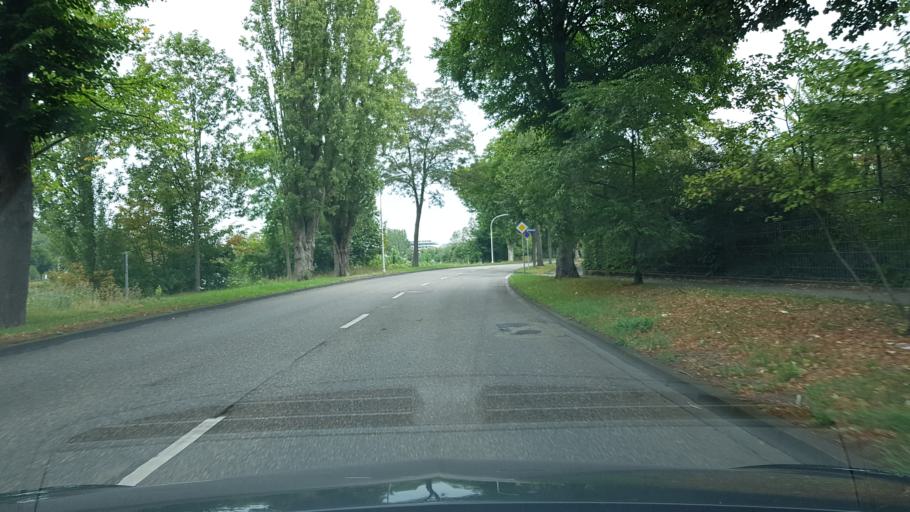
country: DE
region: Rheinland-Pfalz
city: Koblenz
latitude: 50.3516
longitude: 7.5561
